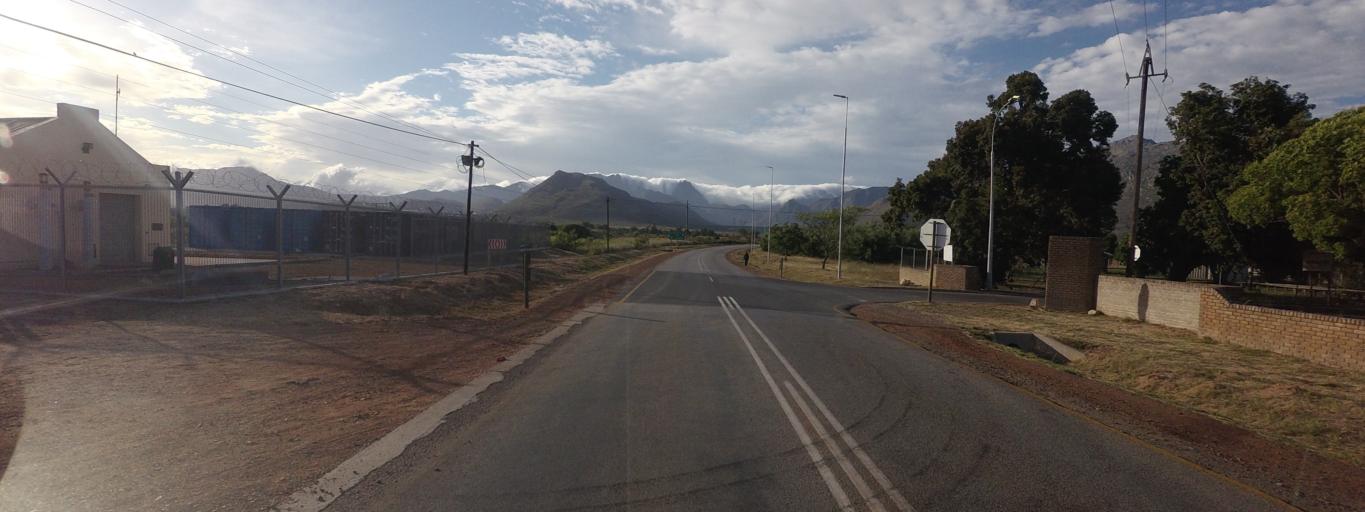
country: ZA
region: Western Cape
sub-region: Cape Winelands District Municipality
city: Paarl
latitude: -33.8717
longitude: 19.0439
